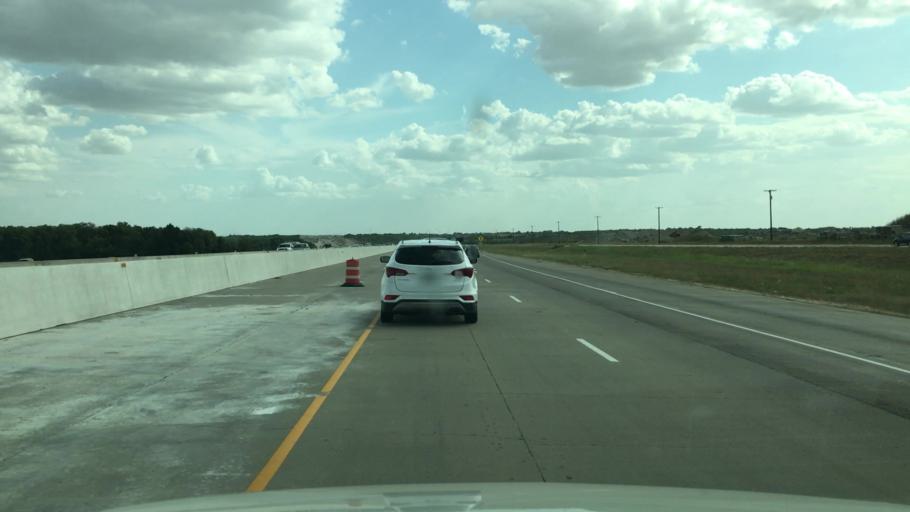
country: US
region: Texas
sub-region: McLennan County
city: Bruceville-Eddy
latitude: 31.2782
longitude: -97.2615
